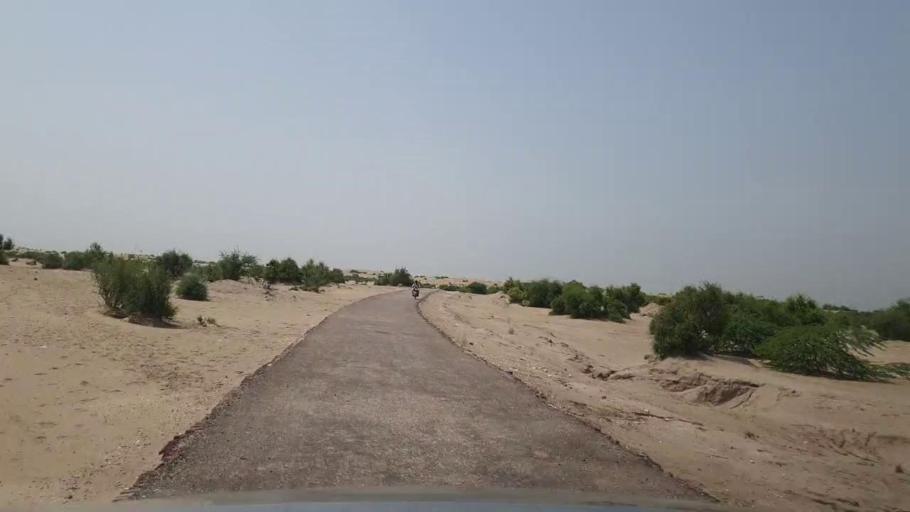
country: PK
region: Sindh
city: Pano Aqil
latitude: 27.6056
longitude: 69.1468
